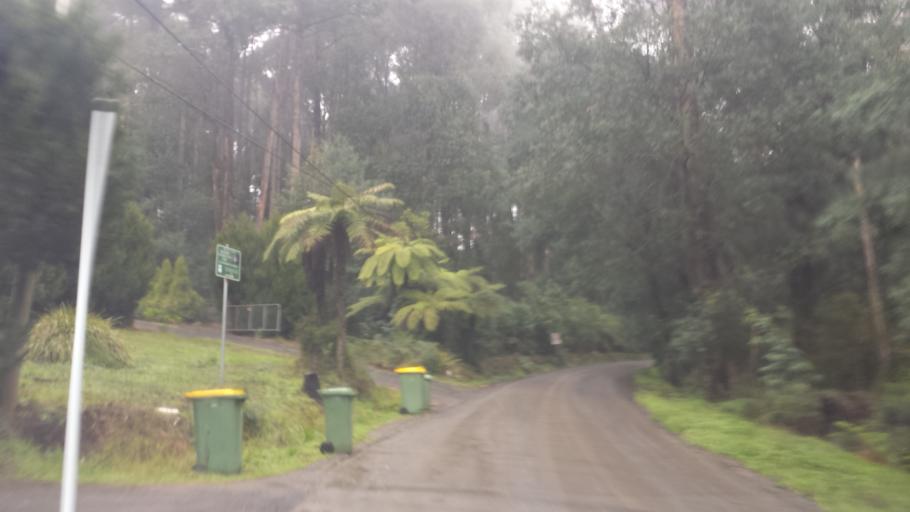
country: AU
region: Victoria
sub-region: Yarra Ranges
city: Monbulk
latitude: -37.8966
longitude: 145.4249
